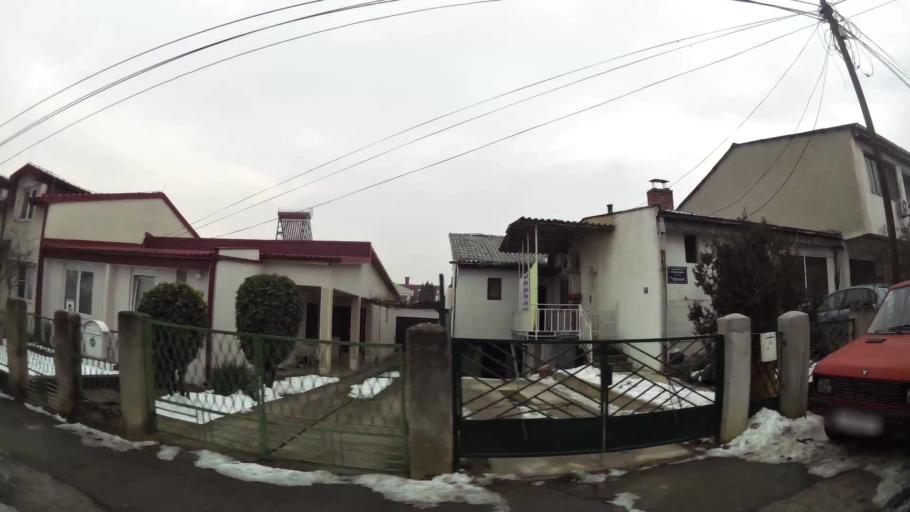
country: MK
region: Cair
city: Cair
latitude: 42.0164
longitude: 21.4558
